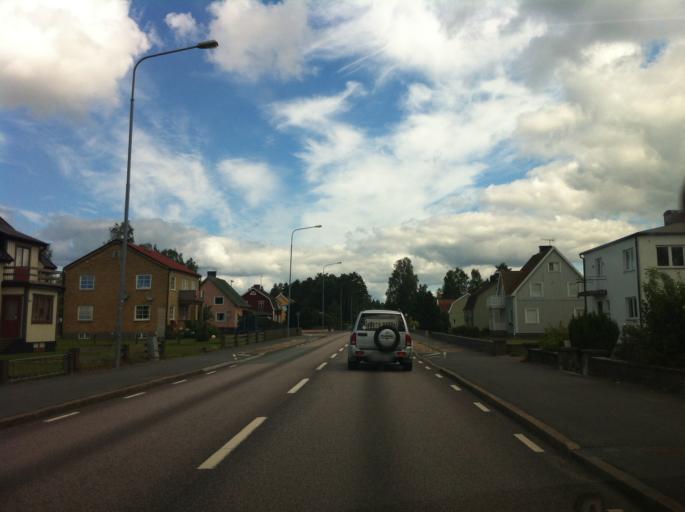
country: SE
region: Joenkoeping
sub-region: Gislaveds Kommun
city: Smalandsstenar
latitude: 57.1705
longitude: 13.4187
